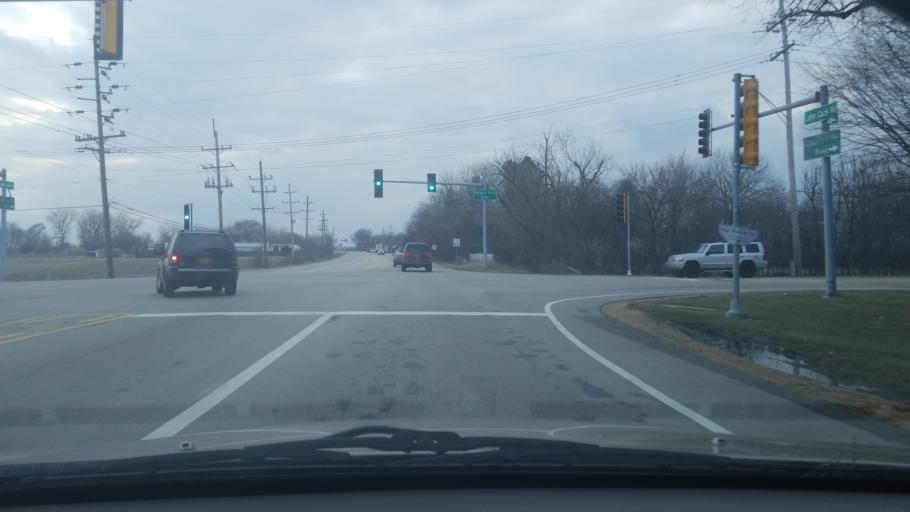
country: US
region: Illinois
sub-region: Kane County
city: Carpentersville
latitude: 42.1541
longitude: -88.2574
